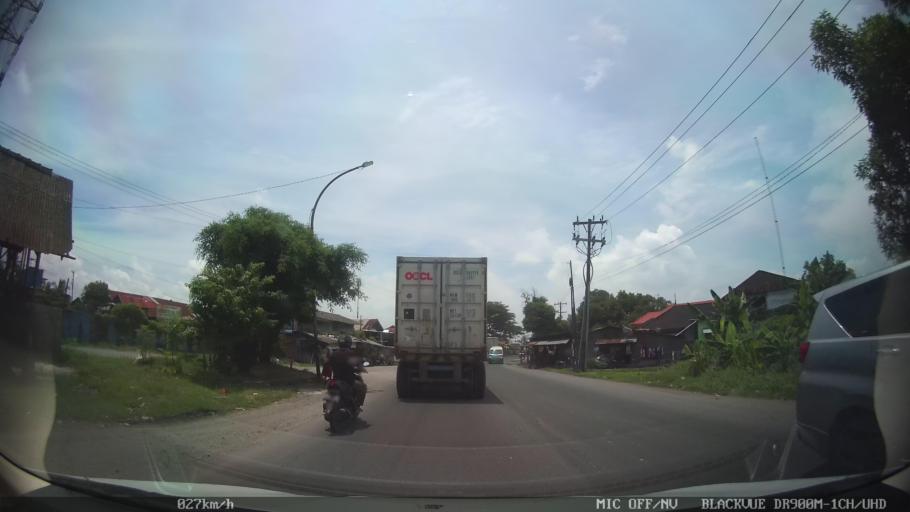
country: ID
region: North Sumatra
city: Belawan
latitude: 3.7533
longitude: 98.6761
